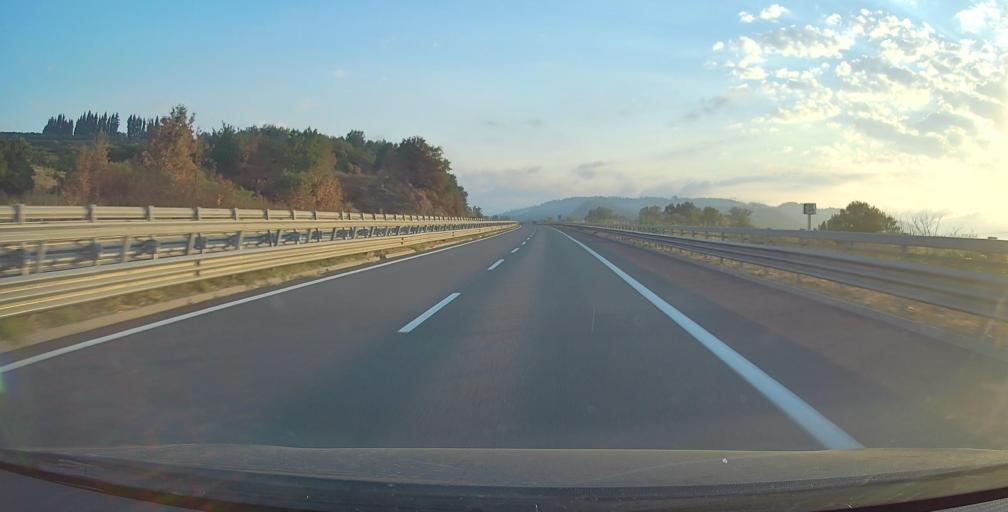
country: IT
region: Calabria
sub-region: Provincia di Reggio Calabria
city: Candidoni
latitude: 38.5154
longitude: 16.0501
